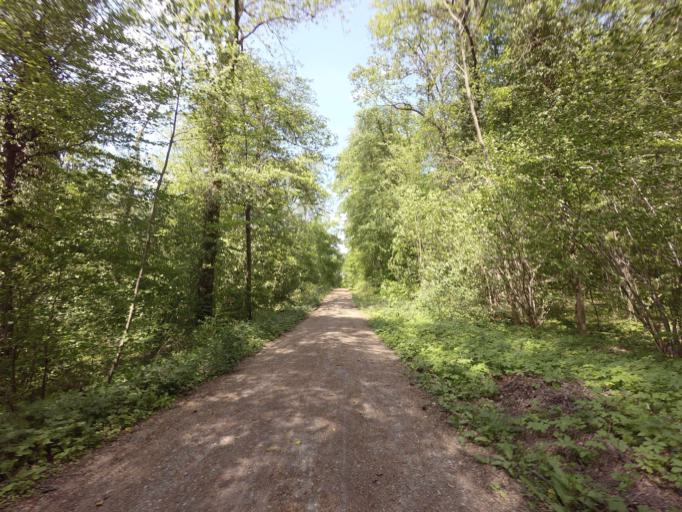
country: DE
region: Lower Saxony
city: Giesen
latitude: 52.1458
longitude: 9.8910
